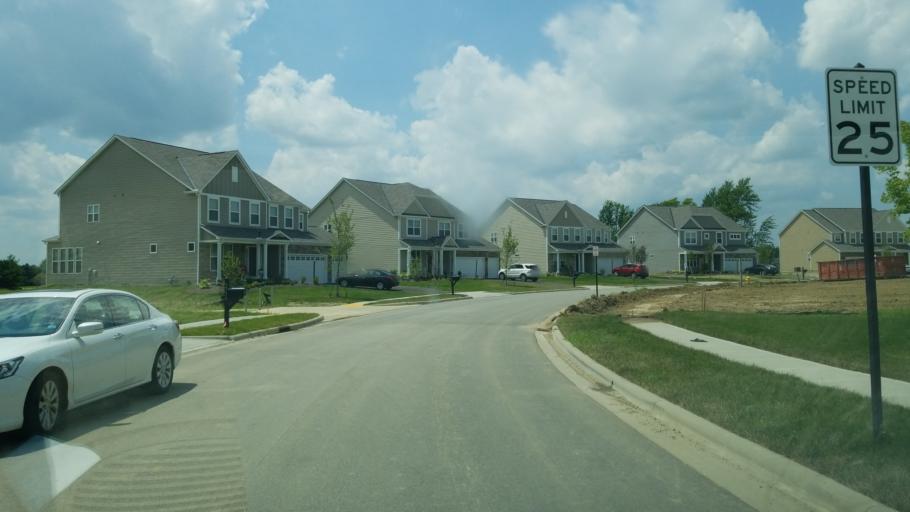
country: US
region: Ohio
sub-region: Delaware County
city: Lewis Center
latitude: 40.2068
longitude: -83.0174
